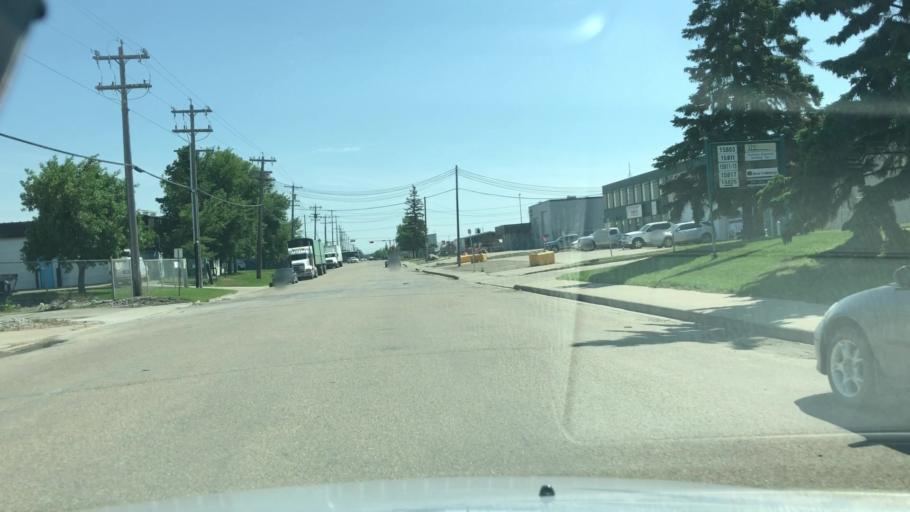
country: CA
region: Alberta
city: St. Albert
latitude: 53.5737
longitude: -113.5950
